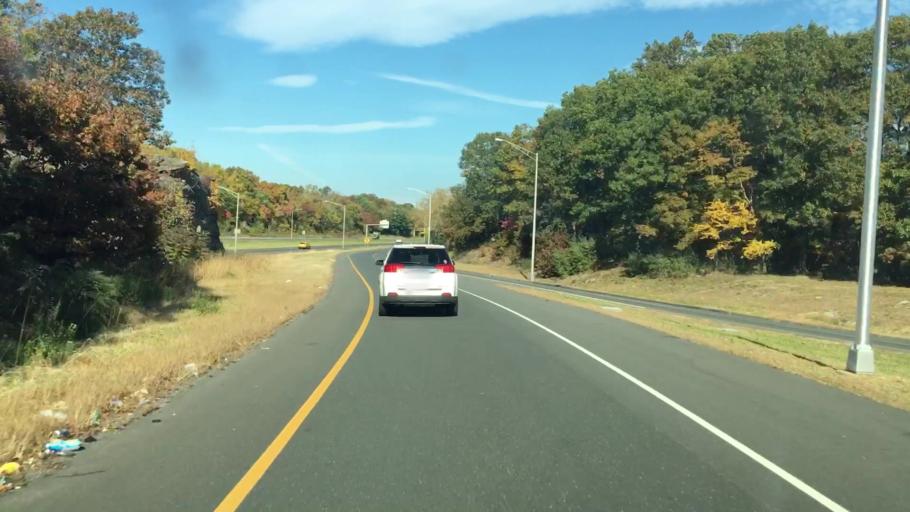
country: US
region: Connecticut
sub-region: Fairfield County
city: Trumbull
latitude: 41.2395
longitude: -73.1516
